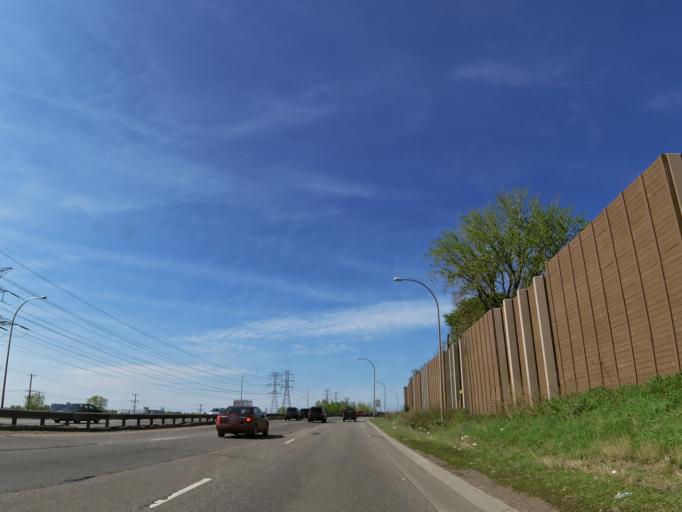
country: US
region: Minnesota
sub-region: Ramsey County
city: Lauderdale
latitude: 44.9940
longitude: -93.2056
